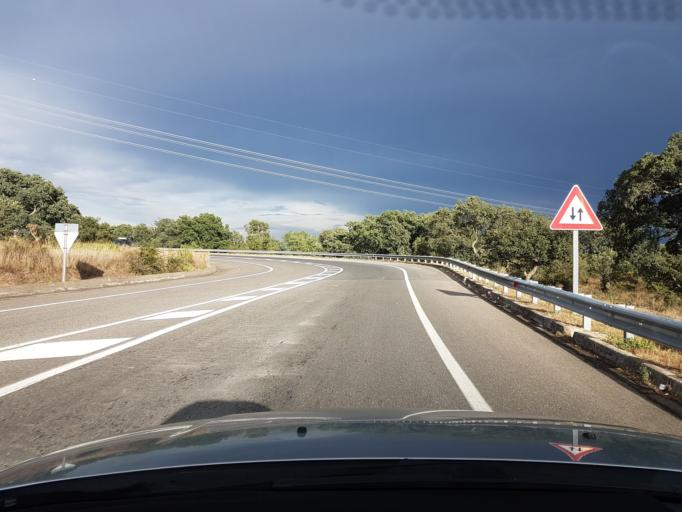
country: IT
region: Sardinia
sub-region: Provincia di Oristano
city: Abbasanta
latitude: 40.1124
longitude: 8.7947
